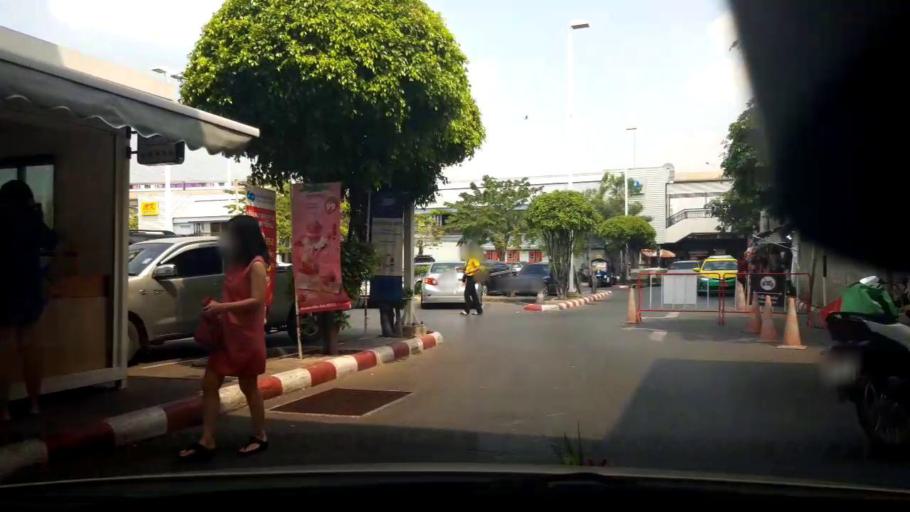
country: TH
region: Bangkok
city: Bang Sue
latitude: 13.8266
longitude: 100.5278
